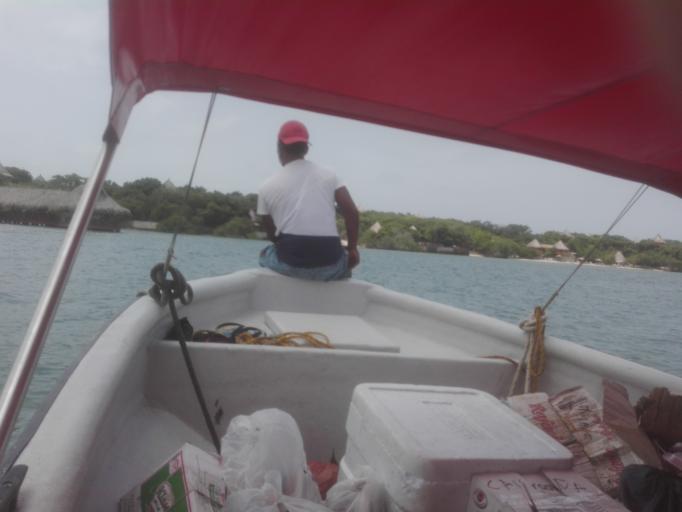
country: CO
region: Bolivar
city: Turbana
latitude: 10.1547
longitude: -75.6868
